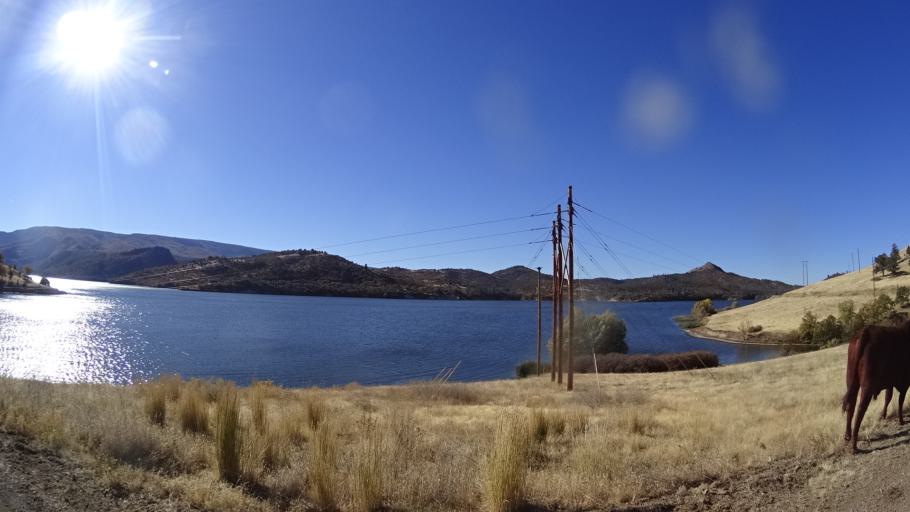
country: US
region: California
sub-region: Siskiyou County
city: Montague
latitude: 41.9914
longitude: -122.3143
